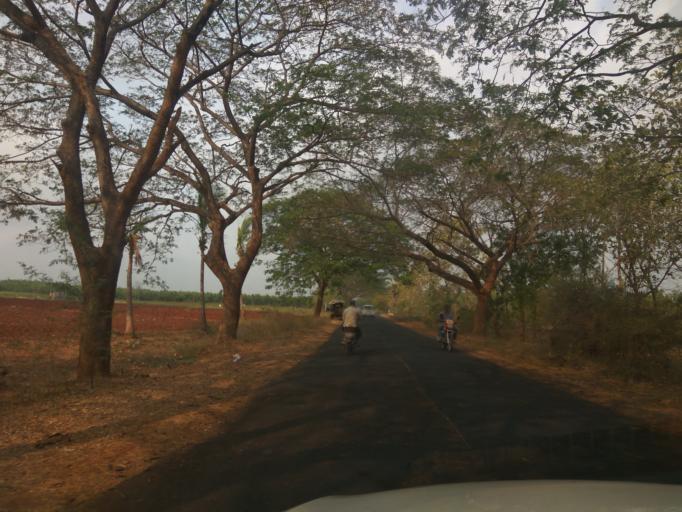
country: IN
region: Andhra Pradesh
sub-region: Prakasam
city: Kandukur
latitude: 15.1997
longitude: 79.8473
